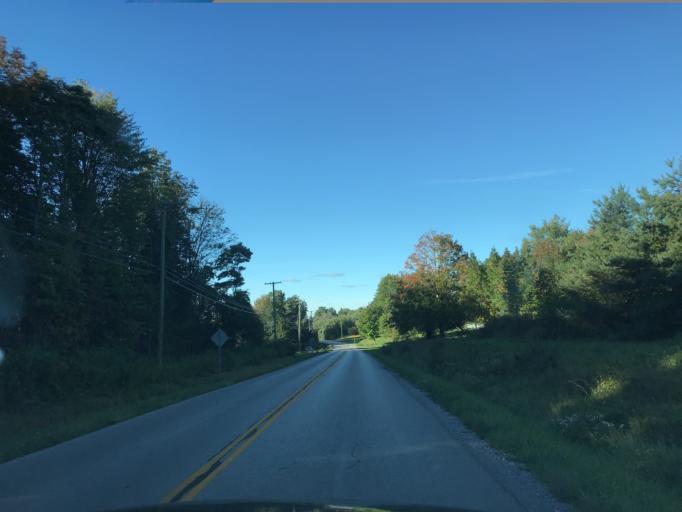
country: US
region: Ohio
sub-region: Ashtabula County
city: Edgewood
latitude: 41.8449
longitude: -80.7559
